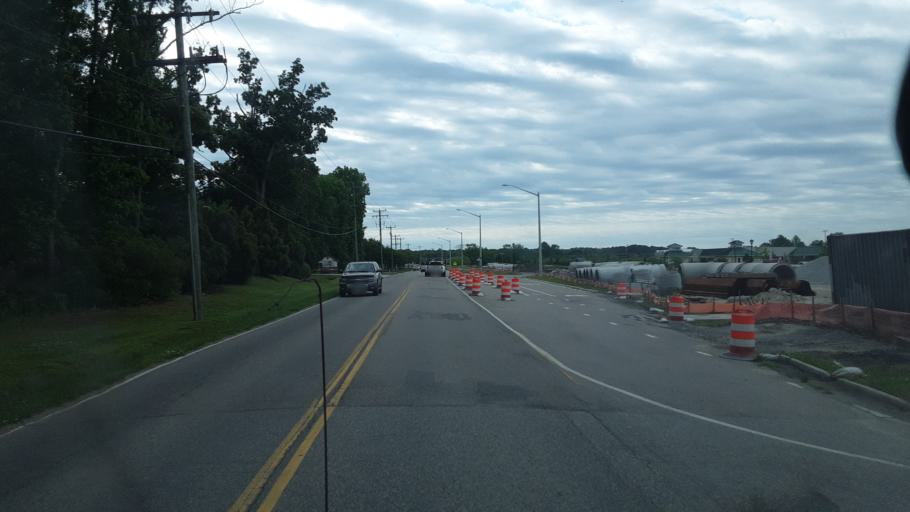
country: US
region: Virginia
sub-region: City of Virginia Beach
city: Virginia Beach
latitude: 36.7497
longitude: -76.0069
